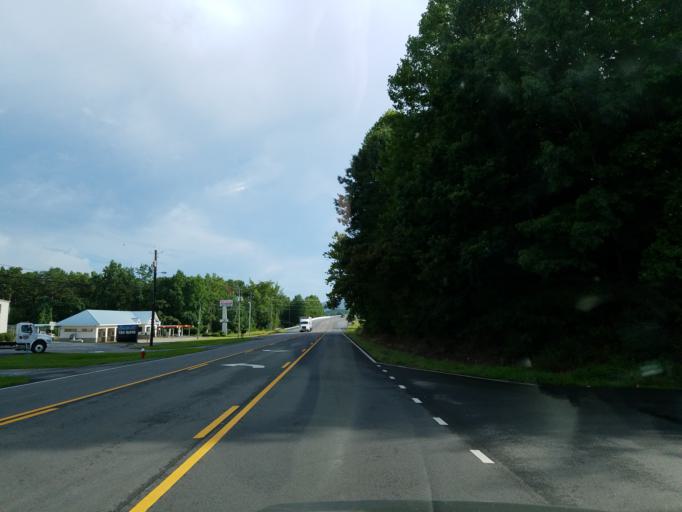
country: US
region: Georgia
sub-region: White County
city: Cleveland
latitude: 34.5832
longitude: -83.7616
